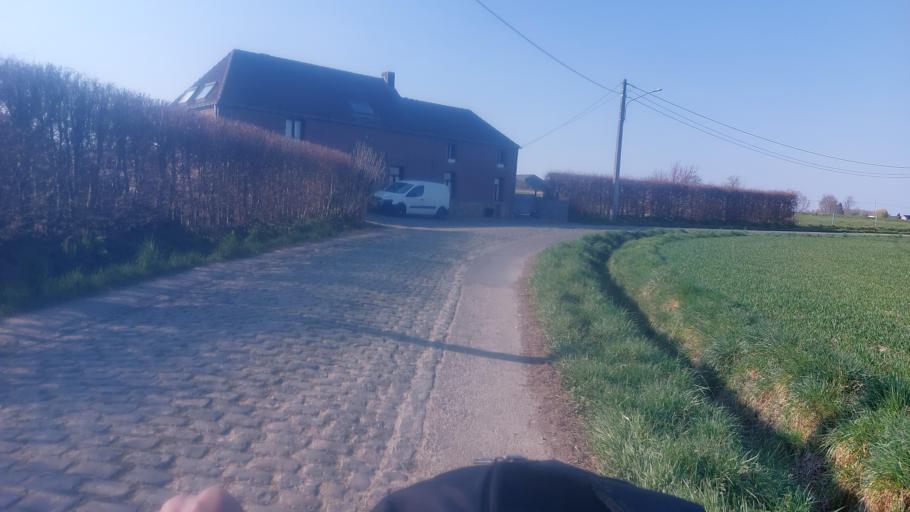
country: BE
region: Wallonia
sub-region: Province du Hainaut
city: Brugelette
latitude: 50.6415
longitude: 3.8410
